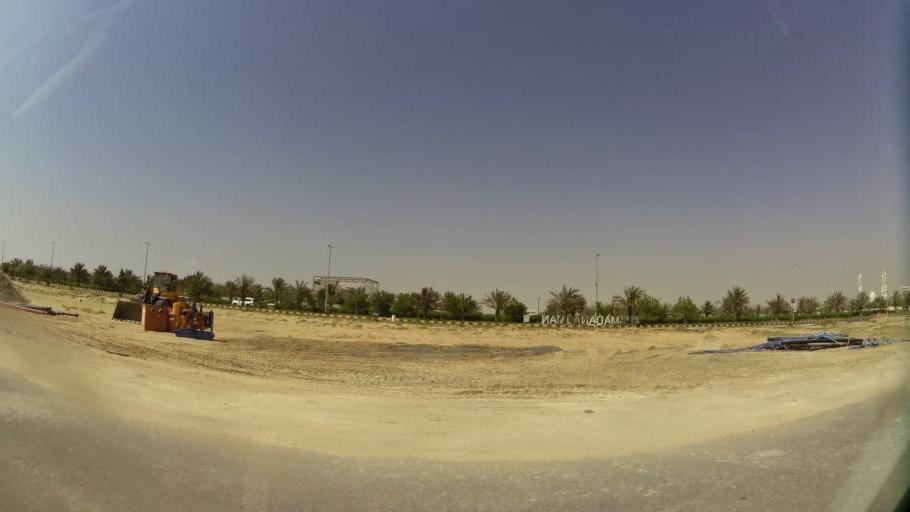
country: AE
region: Ajman
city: Ajman
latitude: 25.4163
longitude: 55.4823
